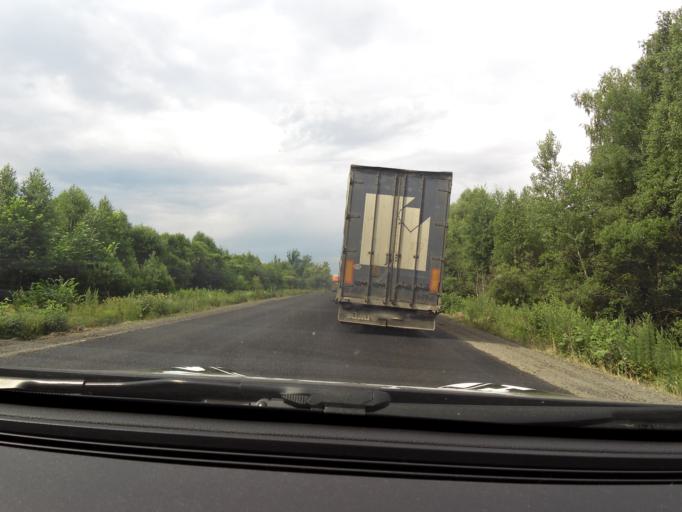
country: RU
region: Chelyabinsk
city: Asha
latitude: 54.8644
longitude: 57.1668
